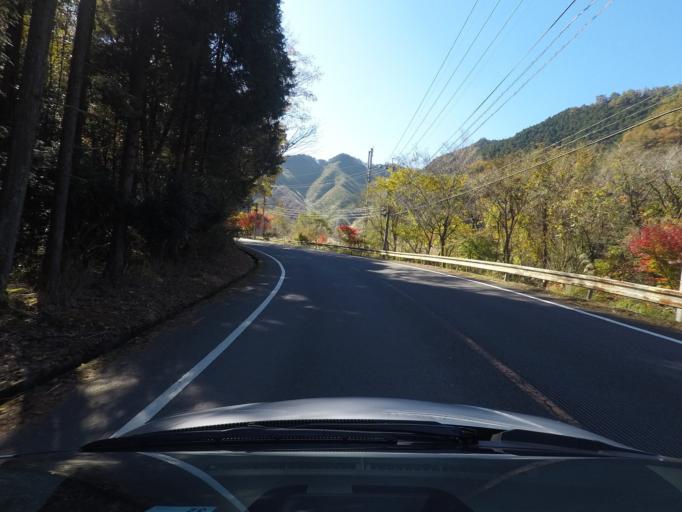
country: JP
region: Miyazaki
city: Kobayashi
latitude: 32.0597
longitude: 131.0762
